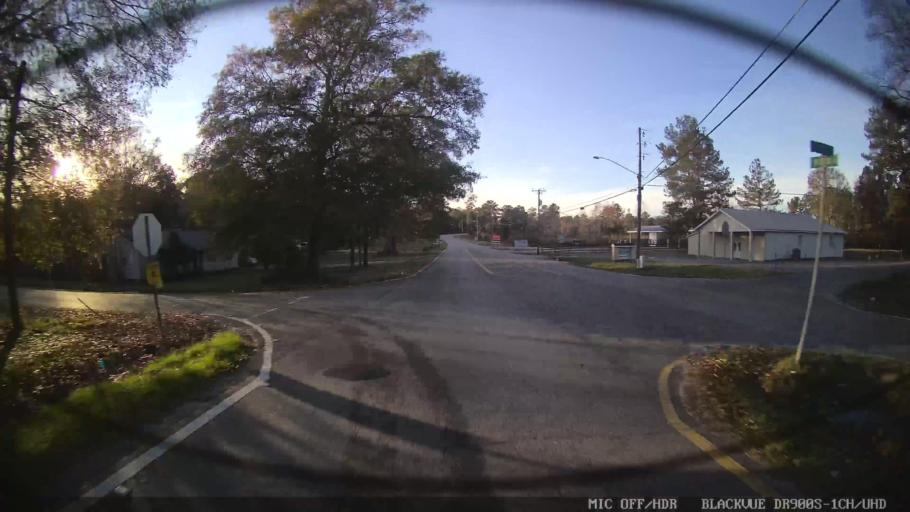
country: US
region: Mississippi
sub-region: Lamar County
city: Lumberton
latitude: 31.0060
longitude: -89.4649
